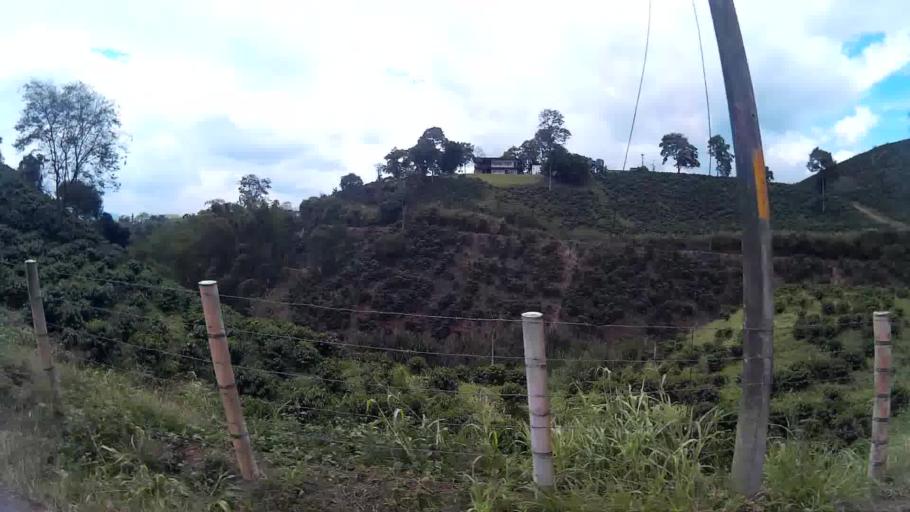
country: CO
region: Risaralda
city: Pereira
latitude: 4.7778
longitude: -75.7194
